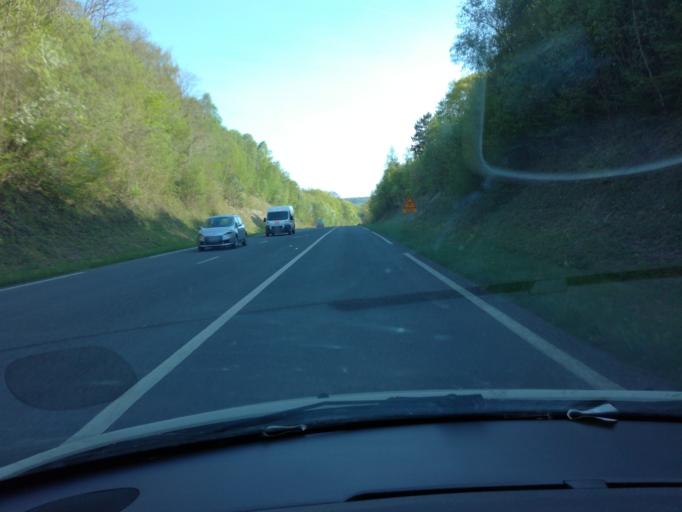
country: FR
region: Picardie
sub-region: Departement de la Somme
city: Poix-de-Picardie
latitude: 49.7887
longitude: 1.9805
